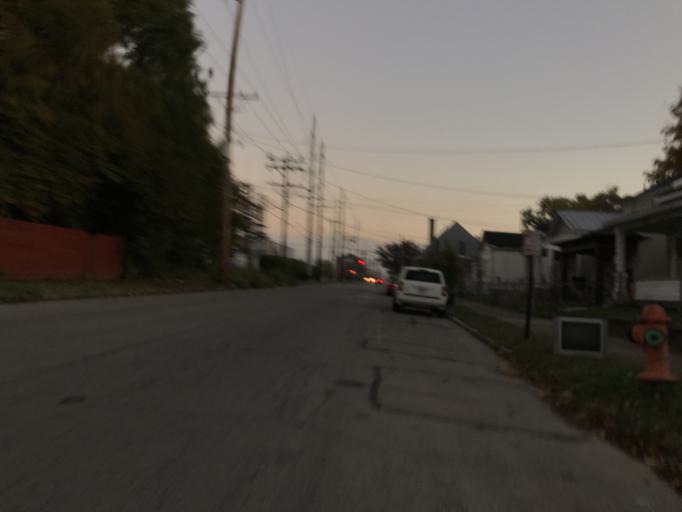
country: US
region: Kentucky
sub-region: Jefferson County
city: Louisville
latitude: 38.2388
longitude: -85.7426
